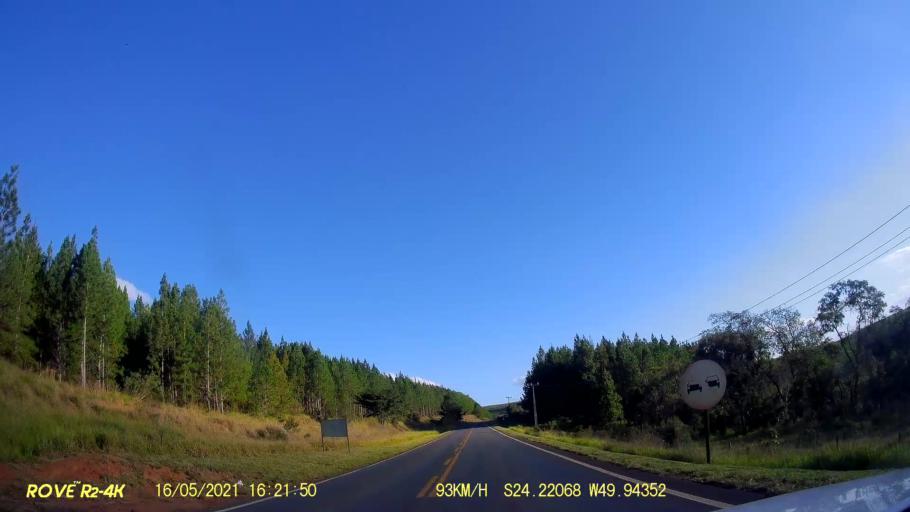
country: BR
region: Parana
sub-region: Jaguariaiva
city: Jaguariaiva
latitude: -24.2209
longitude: -49.9435
